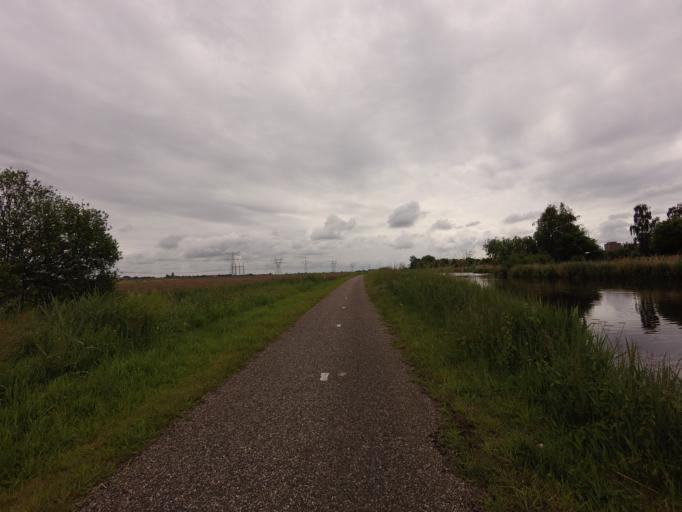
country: NL
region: North Holland
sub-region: Gemeente Waterland
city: Broek in Waterland
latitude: 52.3991
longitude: 4.9646
